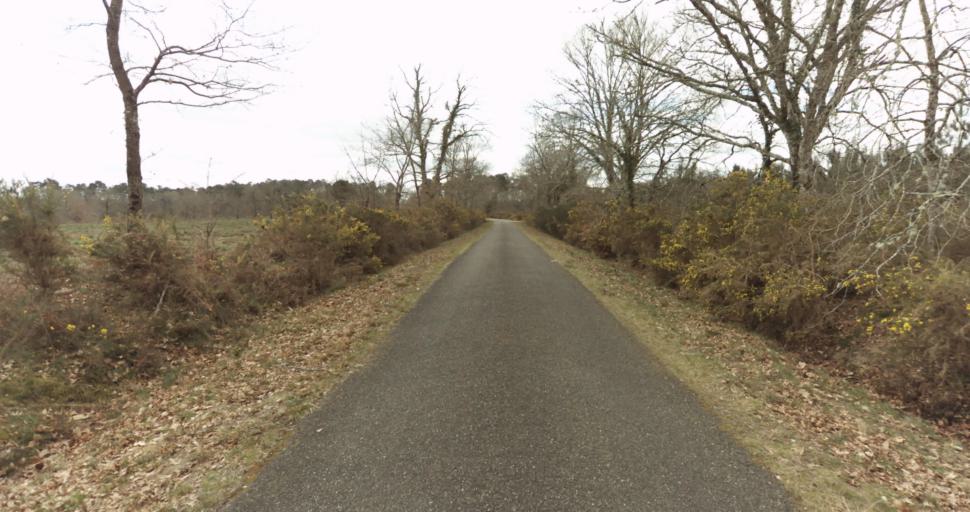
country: FR
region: Aquitaine
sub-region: Departement des Landes
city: Roquefort
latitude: 44.0872
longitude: -0.4416
